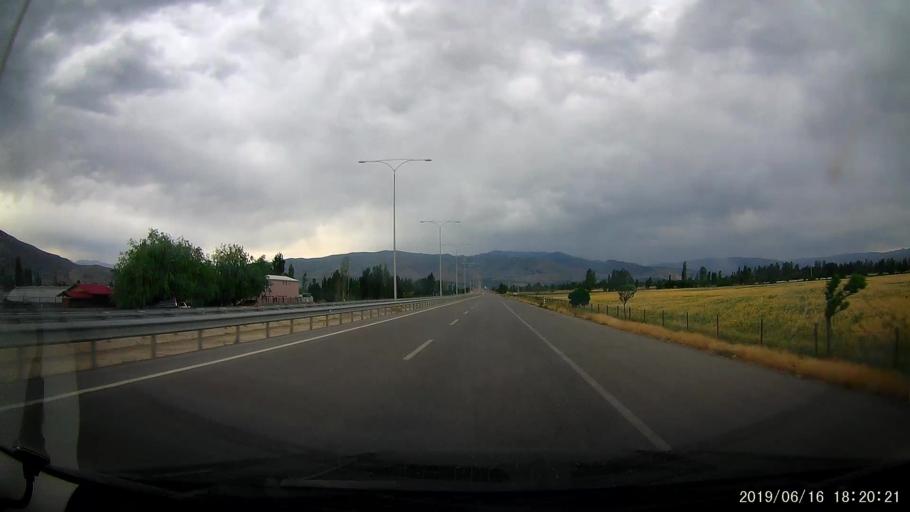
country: TR
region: Erzincan
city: Erzincan
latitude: 39.7196
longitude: 39.4715
